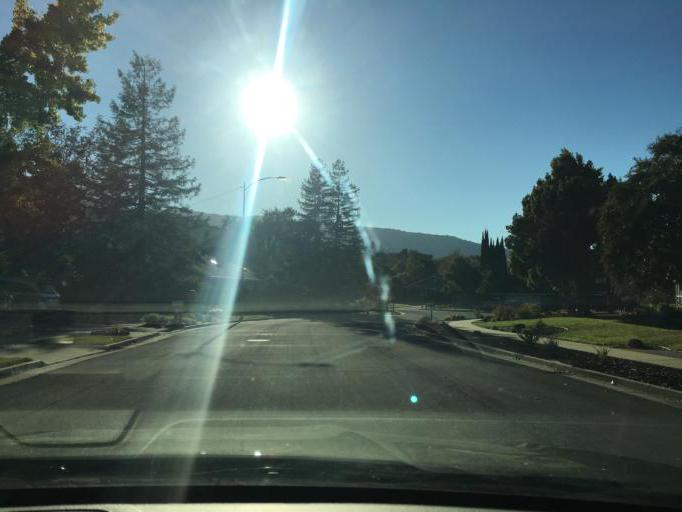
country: US
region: California
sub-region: Santa Clara County
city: Cambrian Park
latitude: 37.2148
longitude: -121.8704
